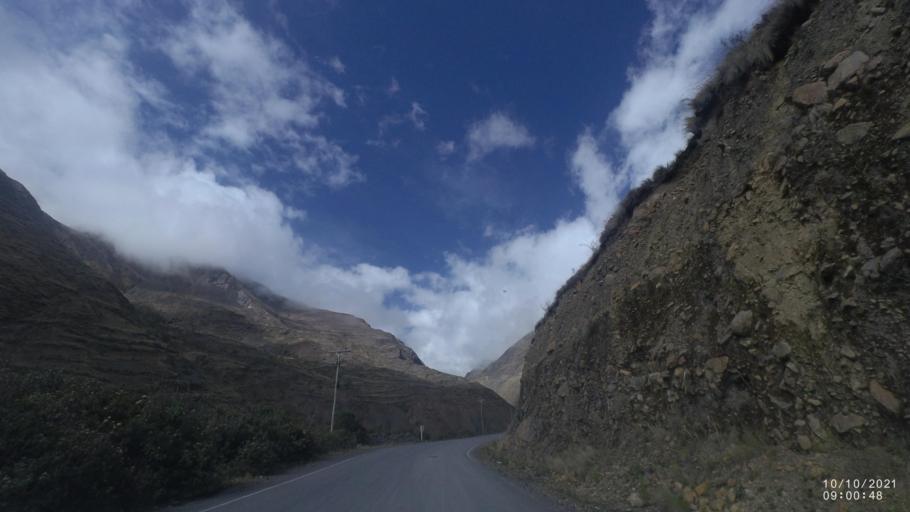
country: BO
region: La Paz
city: Quime
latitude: -16.9988
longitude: -67.2619
